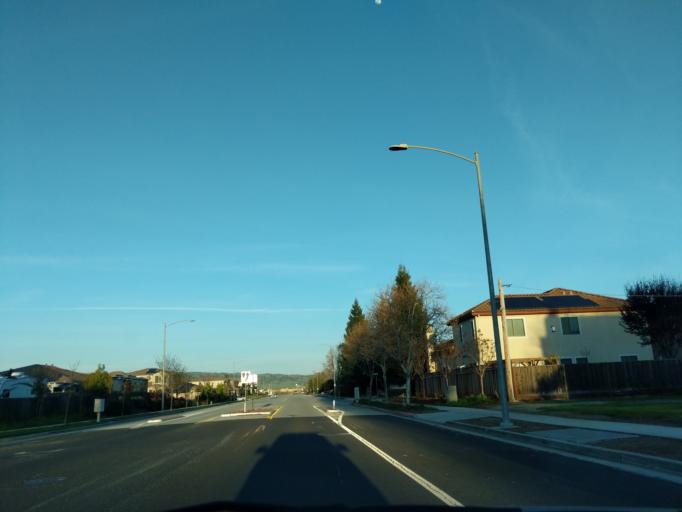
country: US
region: California
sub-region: Santa Clara County
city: Gilroy
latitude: 37.0330
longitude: -121.6025
